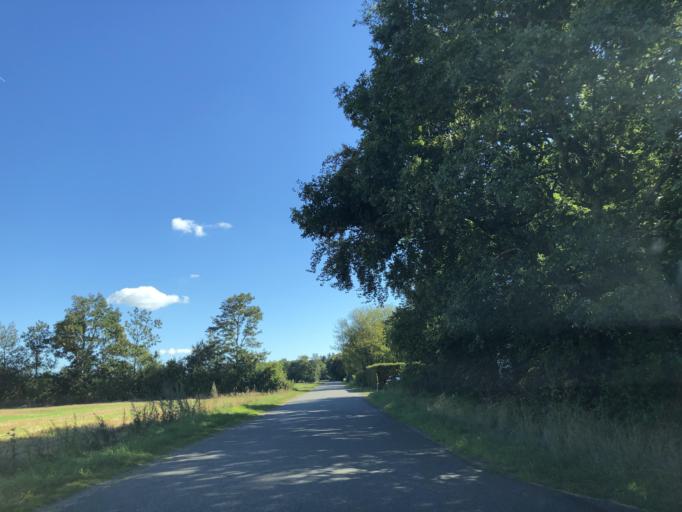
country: DK
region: Central Jutland
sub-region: Viborg Kommune
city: Karup
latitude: 56.3482
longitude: 9.1327
